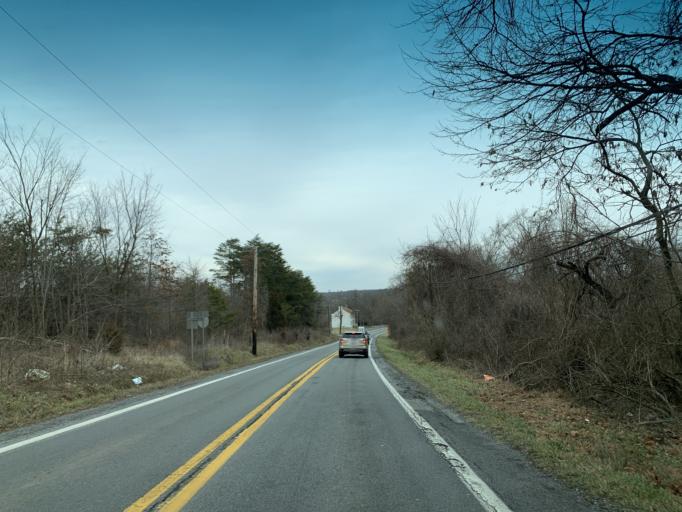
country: US
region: Maryland
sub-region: Washington County
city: Williamsport
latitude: 39.5990
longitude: -77.8361
